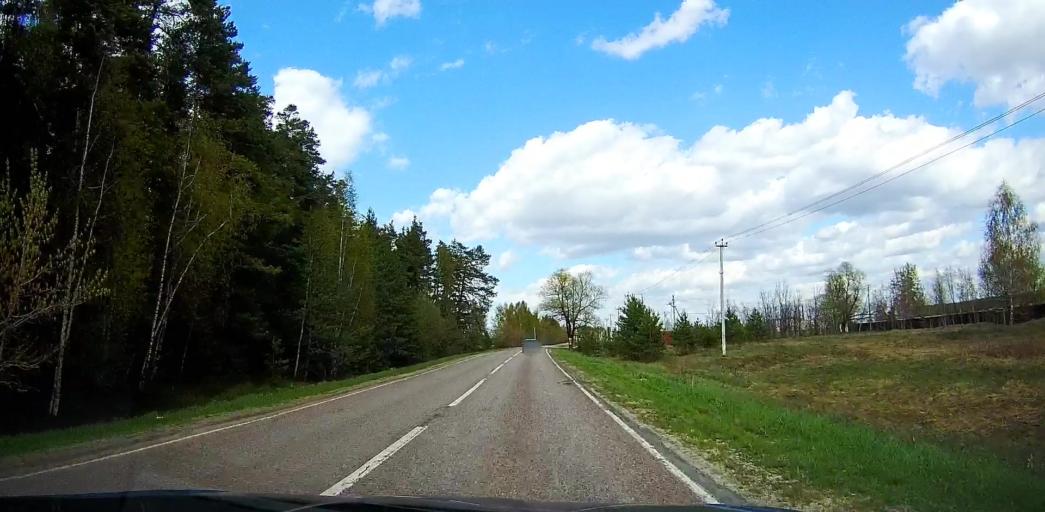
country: RU
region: Moskovskaya
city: Davydovo
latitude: 55.5976
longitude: 38.8393
